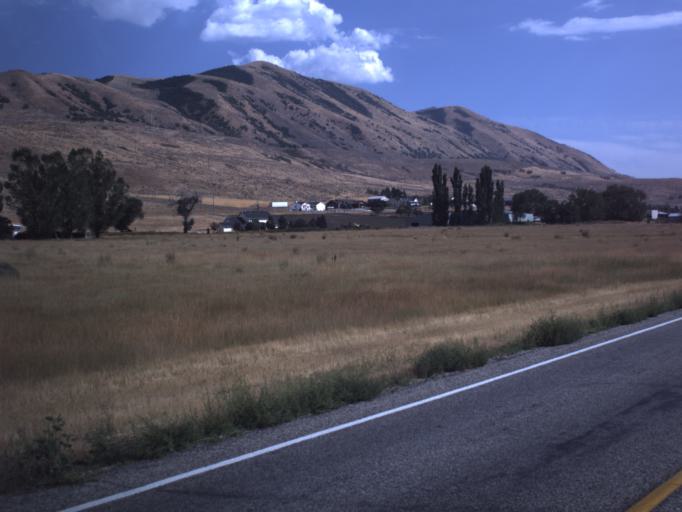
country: US
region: Utah
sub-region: Box Elder County
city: Garland
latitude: 41.7700
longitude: -112.0968
